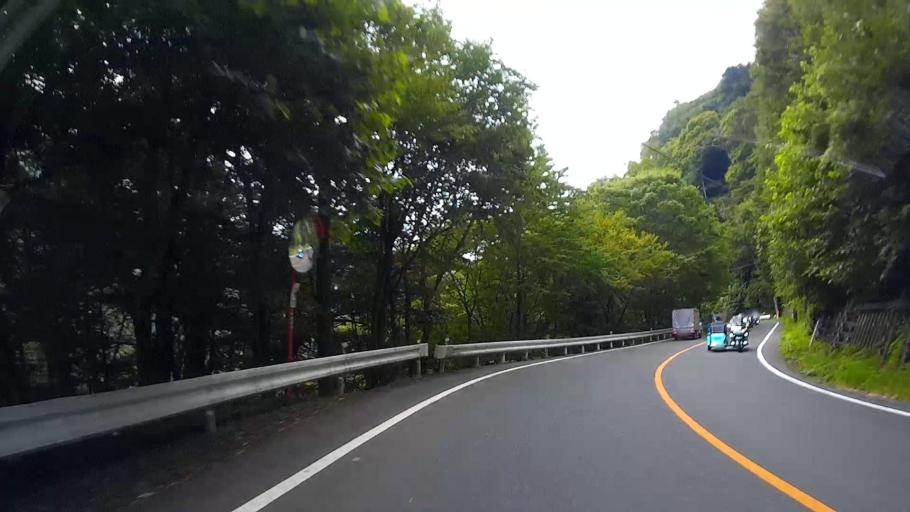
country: JP
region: Yamanashi
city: Enzan
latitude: 35.9180
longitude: 138.8301
